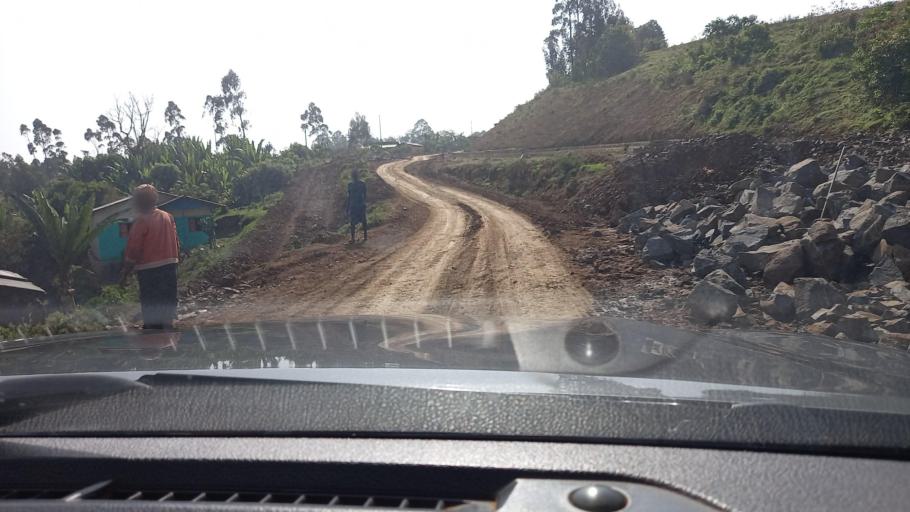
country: ET
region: Southern Nations, Nationalities, and People's Region
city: Mizan Teferi
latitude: 6.1654
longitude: 35.5890
